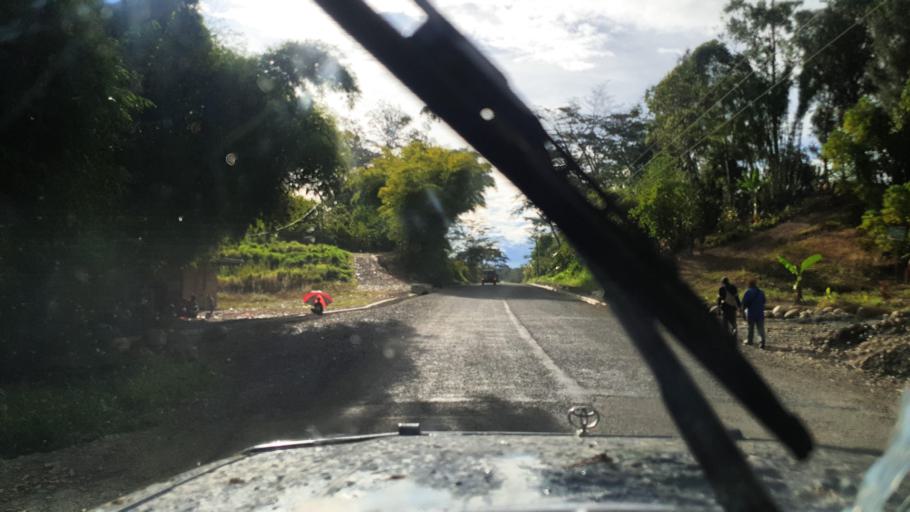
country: PG
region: Jiwaka
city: Minj
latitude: -5.9187
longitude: 144.7672
